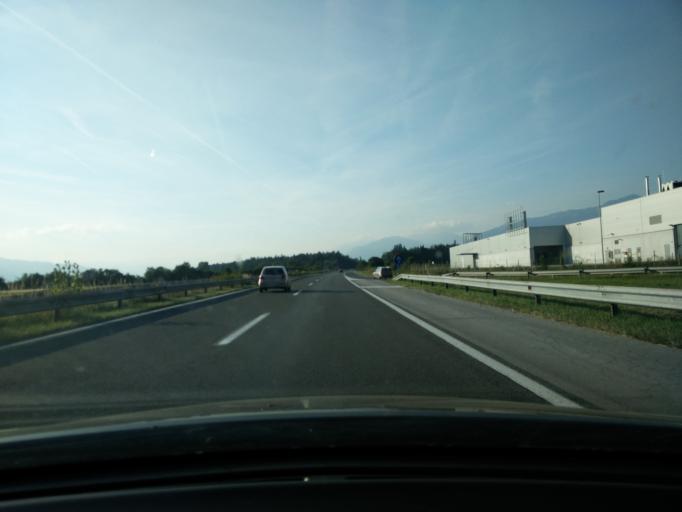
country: SI
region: Sencur
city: Sencur
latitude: 46.2386
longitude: 14.4021
